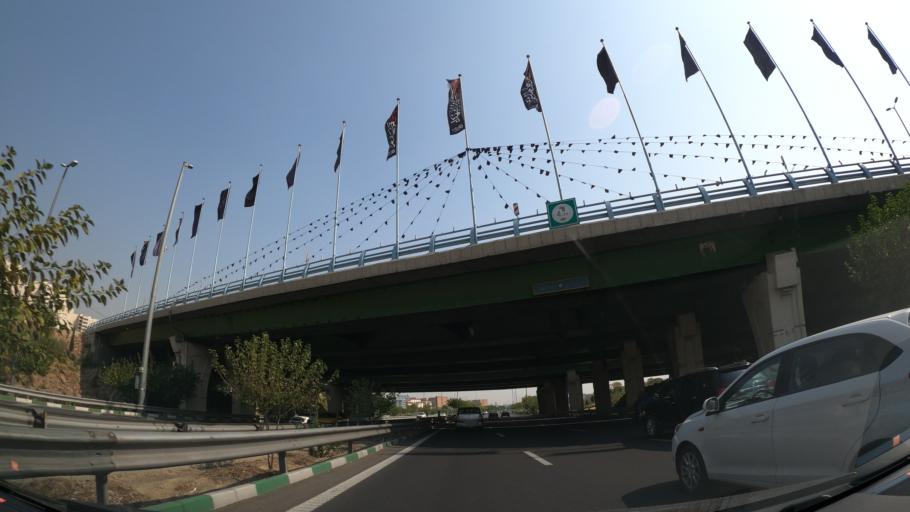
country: IR
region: Tehran
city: Shahr-e Qods
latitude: 35.7600
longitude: 51.2546
